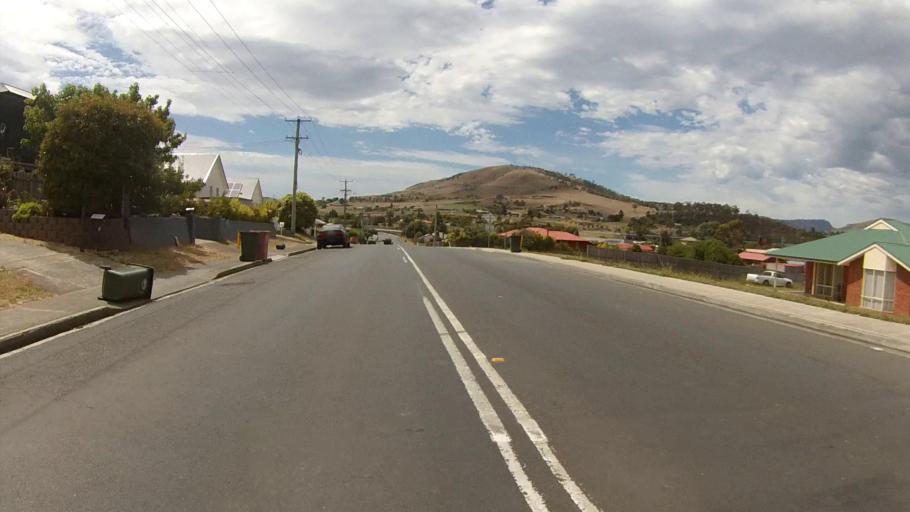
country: AU
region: Tasmania
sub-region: Brighton
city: Bridgewater
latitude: -42.7015
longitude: 147.2612
